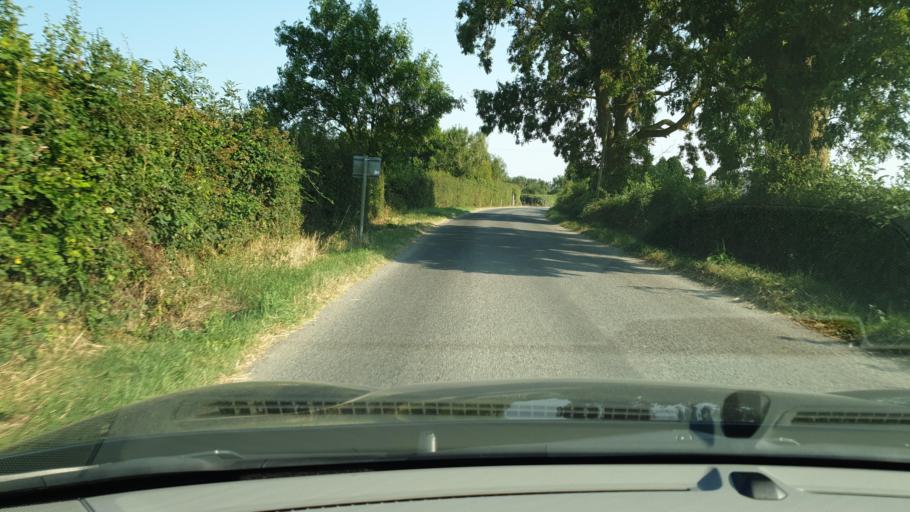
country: IE
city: Kentstown
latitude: 53.6074
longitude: -6.5014
